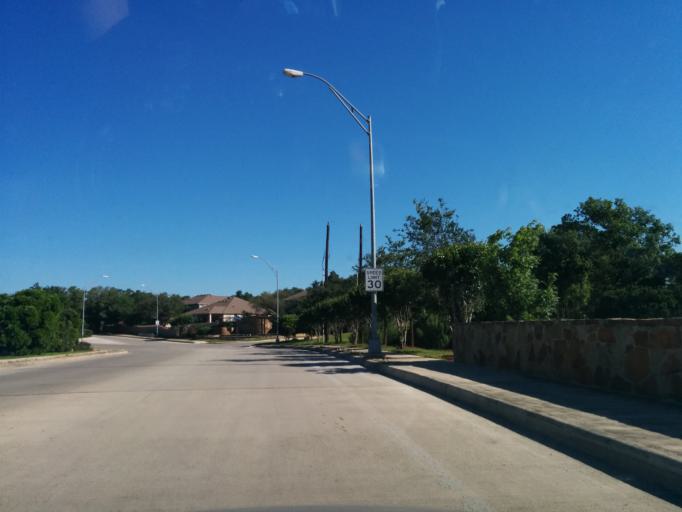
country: US
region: Texas
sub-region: Bexar County
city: Cross Mountain
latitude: 29.6668
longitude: -98.6376
